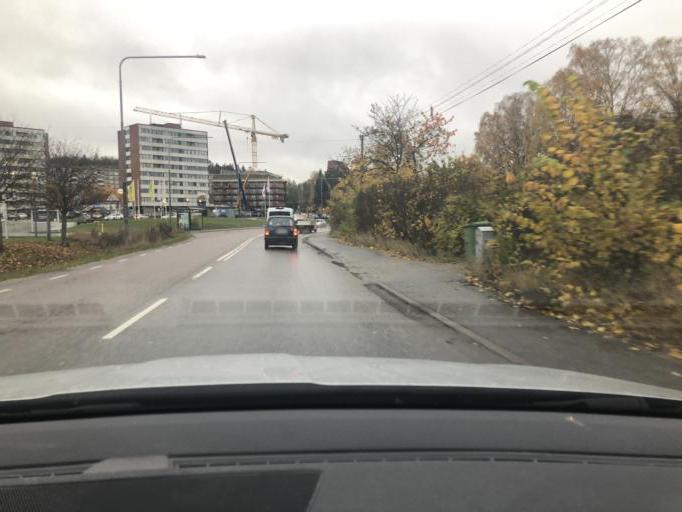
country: SE
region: Stockholm
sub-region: Botkyrka Kommun
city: Fittja
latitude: 59.2530
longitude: 17.8750
